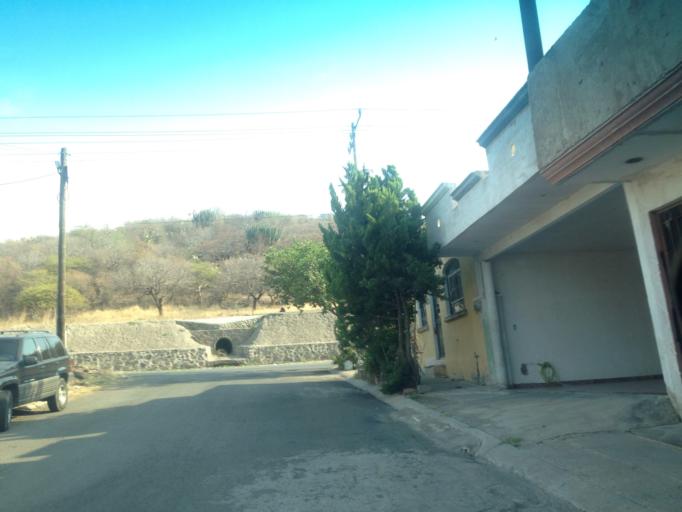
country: MX
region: Jalisco
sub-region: Atotonilco el Alto
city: Vistas del Maguey [Fraccionamiento]
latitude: 20.5280
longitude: -102.5301
